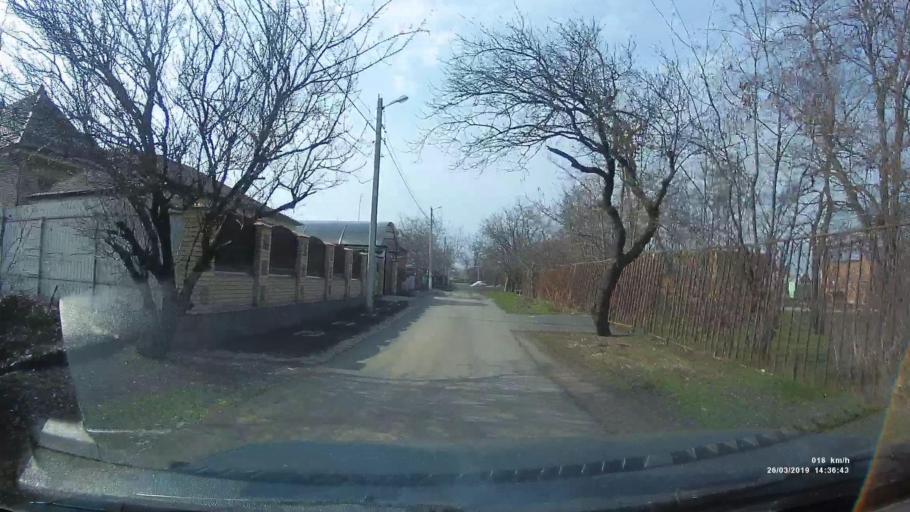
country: RU
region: Rostov
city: Novobessergenovka
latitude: 47.1844
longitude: 38.8690
